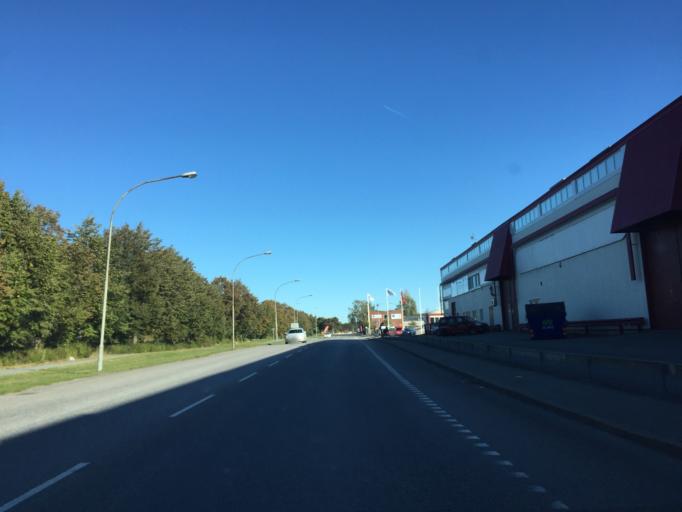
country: SE
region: OErebro
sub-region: Orebro Kommun
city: Orebro
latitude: 59.2637
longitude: 15.1857
